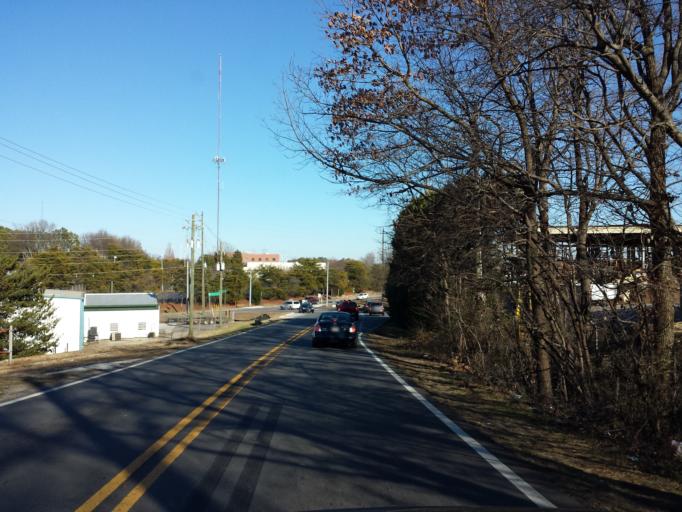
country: US
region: Georgia
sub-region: Cobb County
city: Marietta
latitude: 33.9791
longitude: -84.5599
